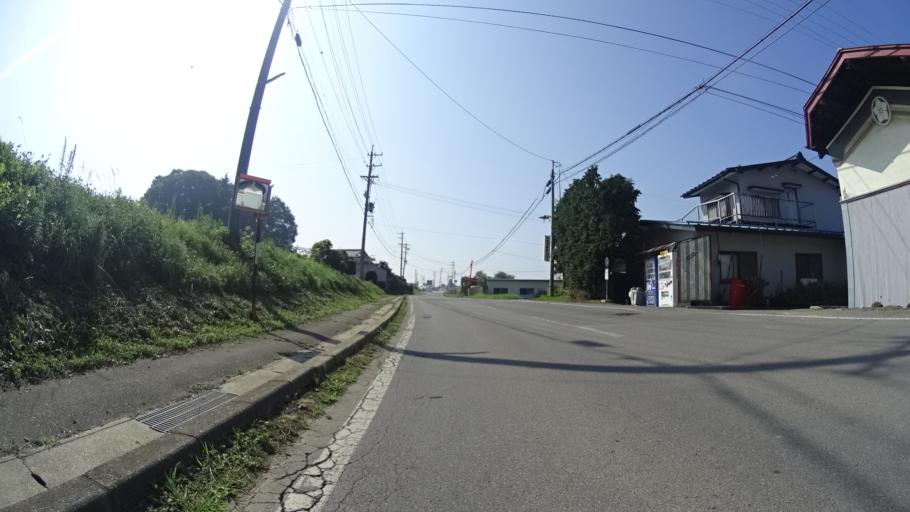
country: JP
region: Nagano
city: Chino
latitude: 35.9495
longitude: 138.2397
